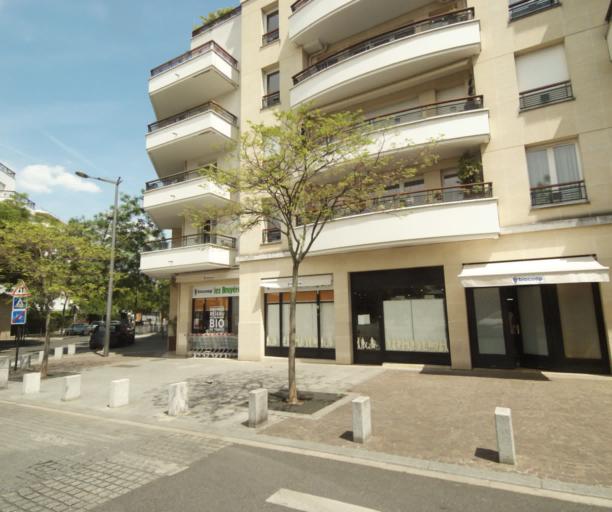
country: FR
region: Ile-de-France
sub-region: Departement des Hauts-de-Seine
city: Courbevoie
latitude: 48.9082
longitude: 2.2612
